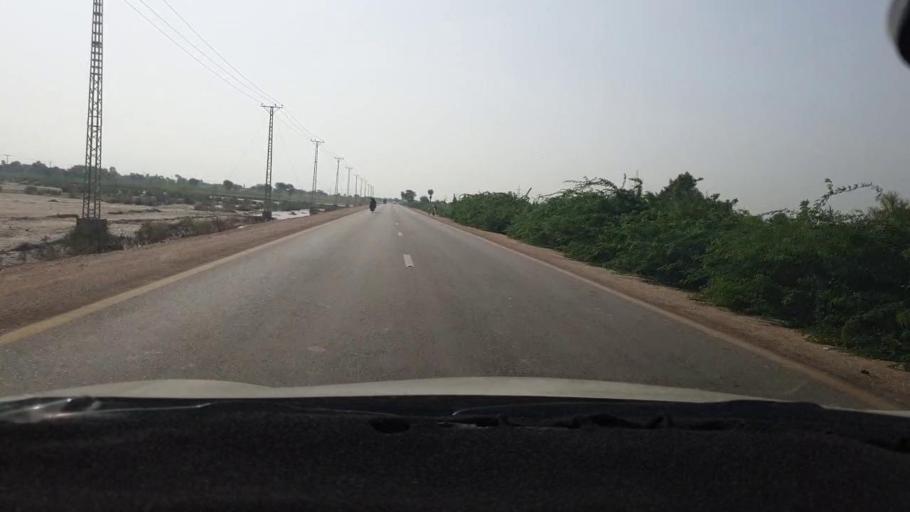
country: PK
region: Sindh
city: Jhol
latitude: 25.9374
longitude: 68.9898
